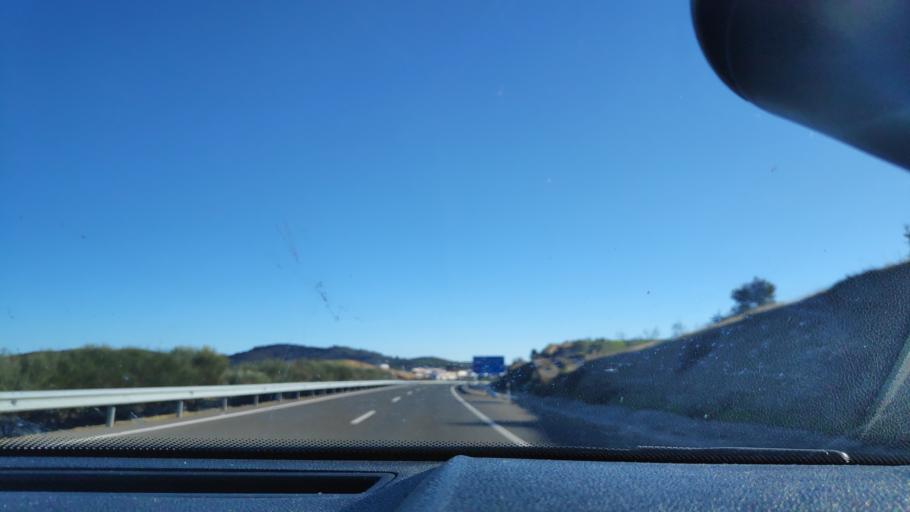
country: ES
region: Extremadura
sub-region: Provincia de Badajoz
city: Monesterio
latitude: 38.0939
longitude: -6.2647
